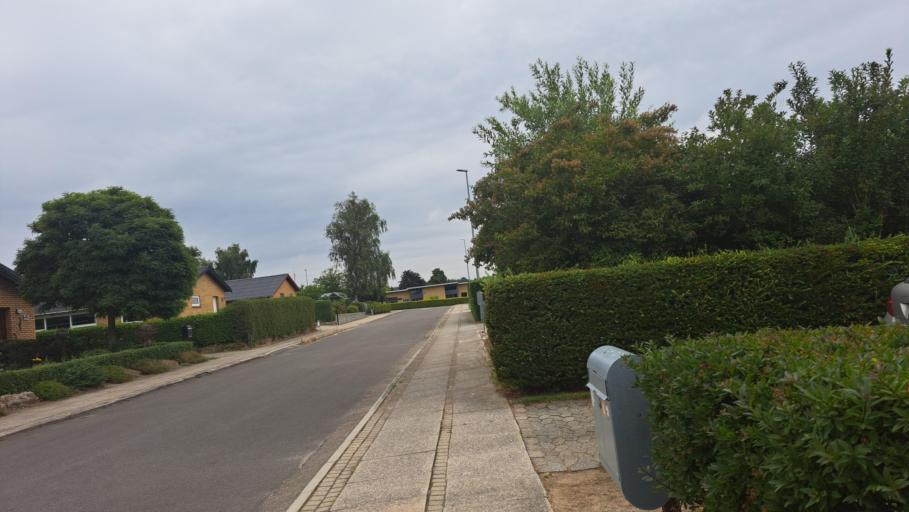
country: DK
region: Central Jutland
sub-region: Hedensted Kommune
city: Hedensted
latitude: 55.7733
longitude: 9.7104
